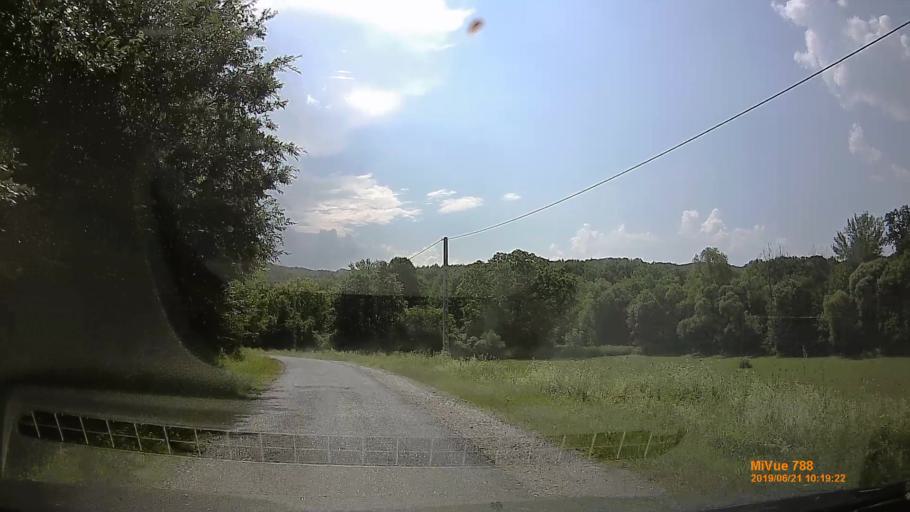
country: HU
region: Baranya
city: Buekkoesd
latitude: 46.1993
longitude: 17.9698
